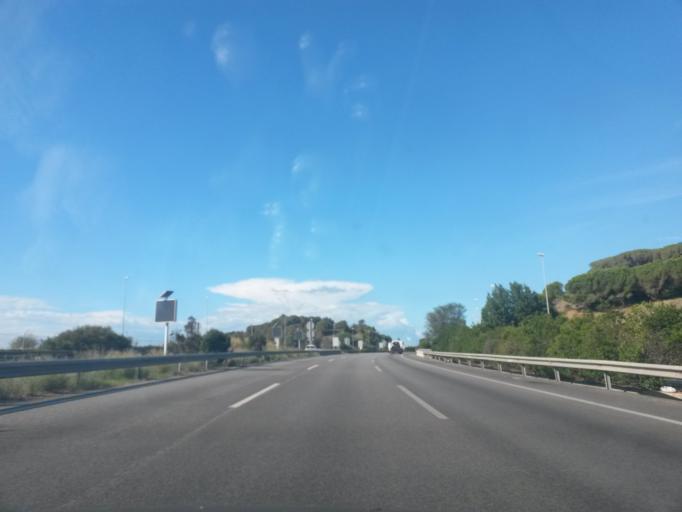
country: ES
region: Catalonia
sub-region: Provincia de Barcelona
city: Arenys de Mar
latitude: 41.5844
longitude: 2.5367
